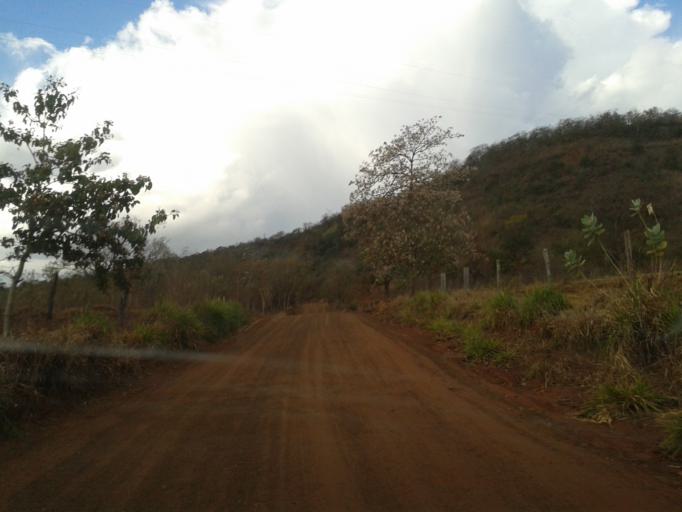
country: BR
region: Minas Gerais
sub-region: Santa Vitoria
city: Santa Vitoria
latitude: -19.2032
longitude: -49.8854
